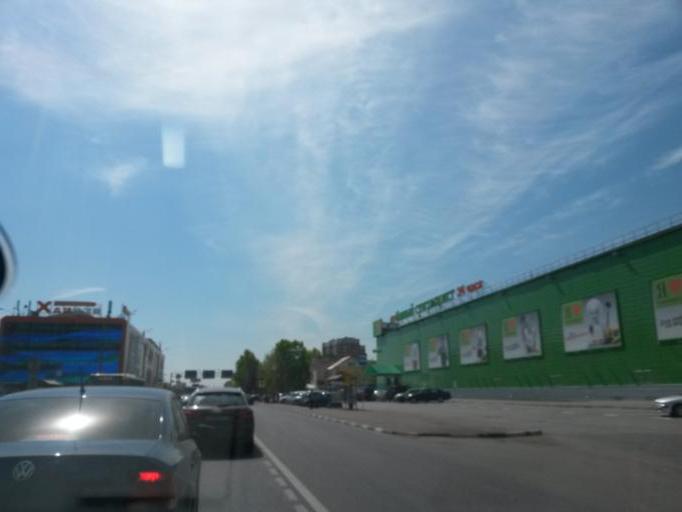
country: RU
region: Moskovskaya
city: Shcherbinka
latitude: 55.5044
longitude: 37.5725
